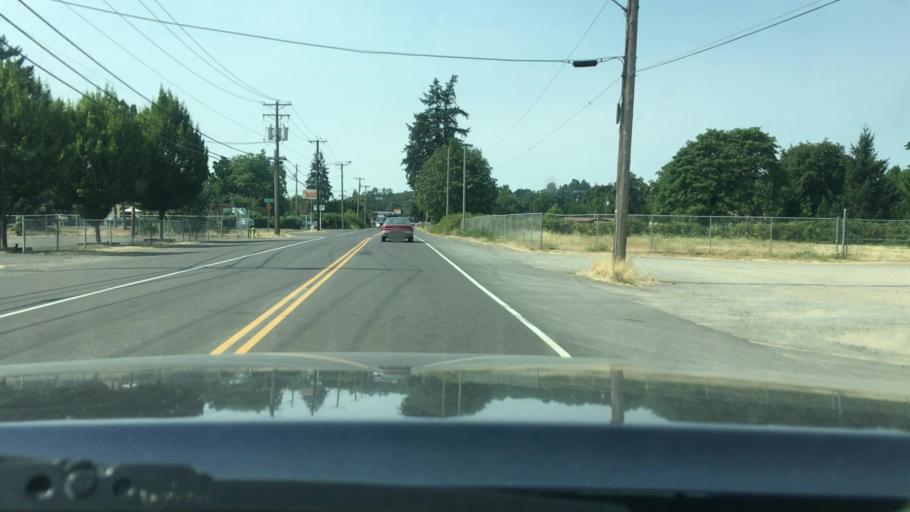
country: US
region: Oregon
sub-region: Lane County
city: Springfield
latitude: 44.0384
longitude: -123.0277
